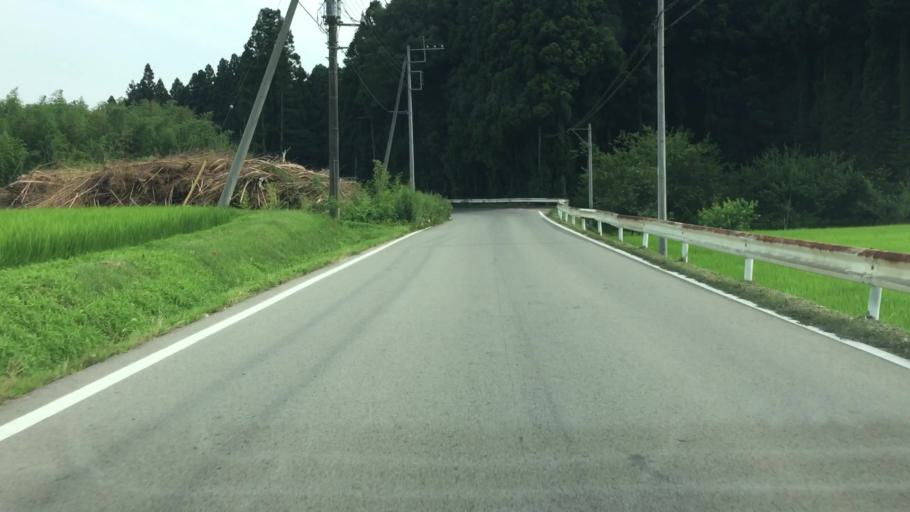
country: JP
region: Tochigi
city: Kuroiso
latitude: 36.9633
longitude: 139.9807
